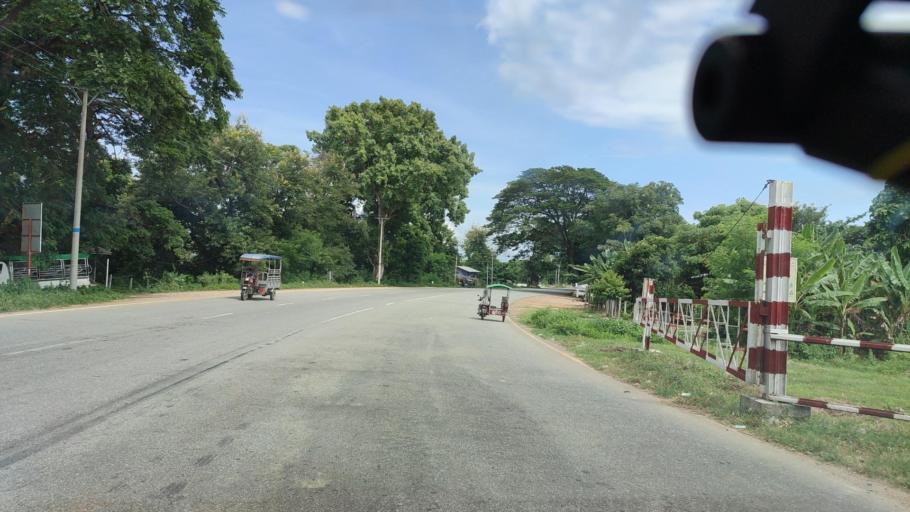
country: MM
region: Mandalay
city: Yamethin
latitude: 20.2194
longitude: 96.1812
